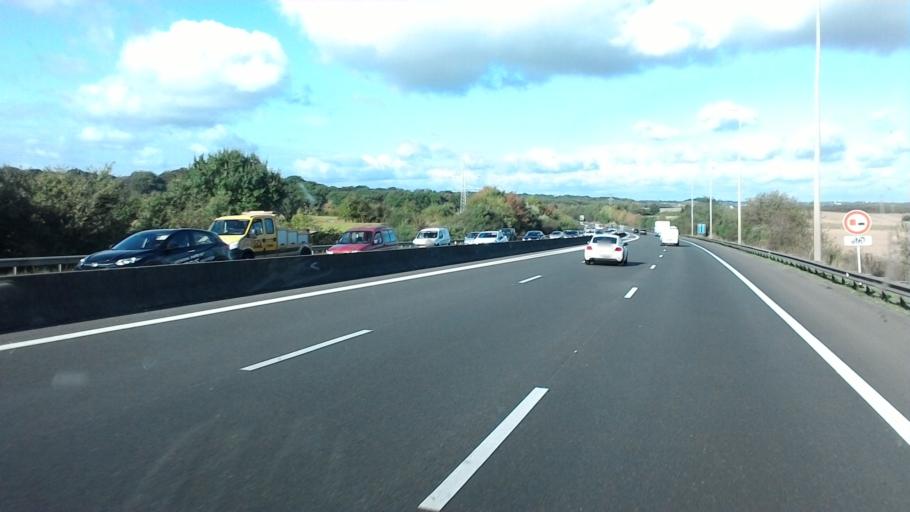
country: LU
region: Luxembourg
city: Crauthem
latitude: 49.5468
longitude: 6.1239
